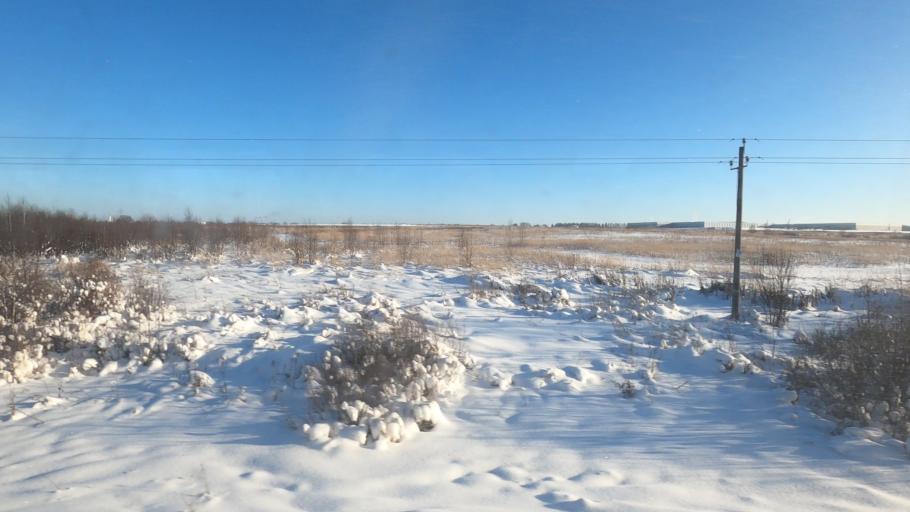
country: RU
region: Moskovskaya
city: Orud'yevo
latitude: 56.4270
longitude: 37.4986
